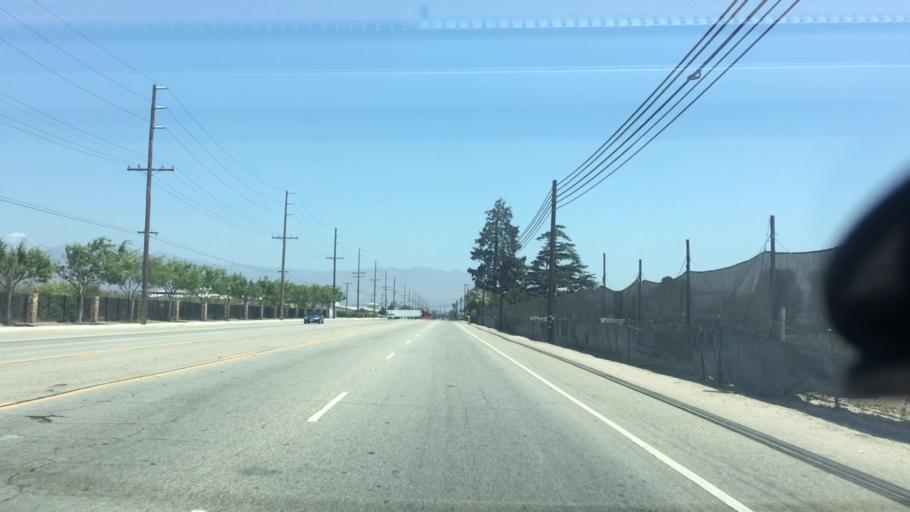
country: US
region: California
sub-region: Ventura County
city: El Rio
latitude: 34.2465
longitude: -119.1621
